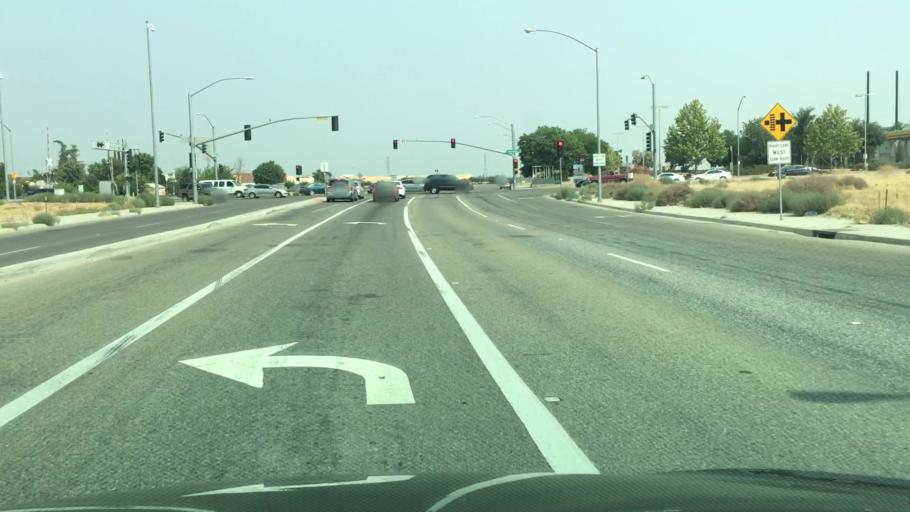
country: US
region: California
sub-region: Fresno County
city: Biola
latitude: 36.8344
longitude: -119.9167
